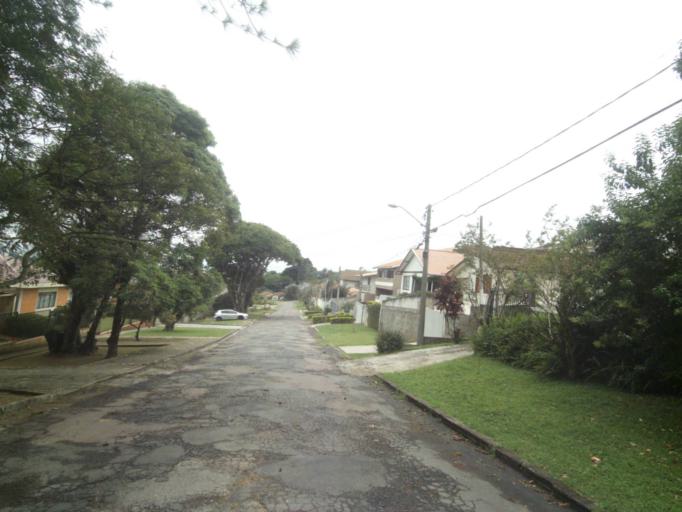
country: BR
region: Parana
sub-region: Curitiba
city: Curitiba
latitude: -25.4084
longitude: -49.2910
